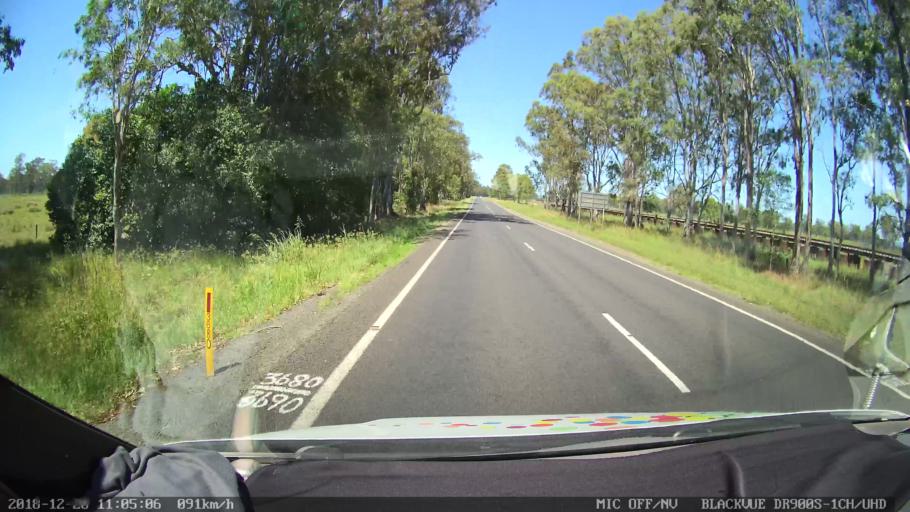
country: AU
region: New South Wales
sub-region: Richmond Valley
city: Casino
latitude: -28.8926
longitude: 153.0437
